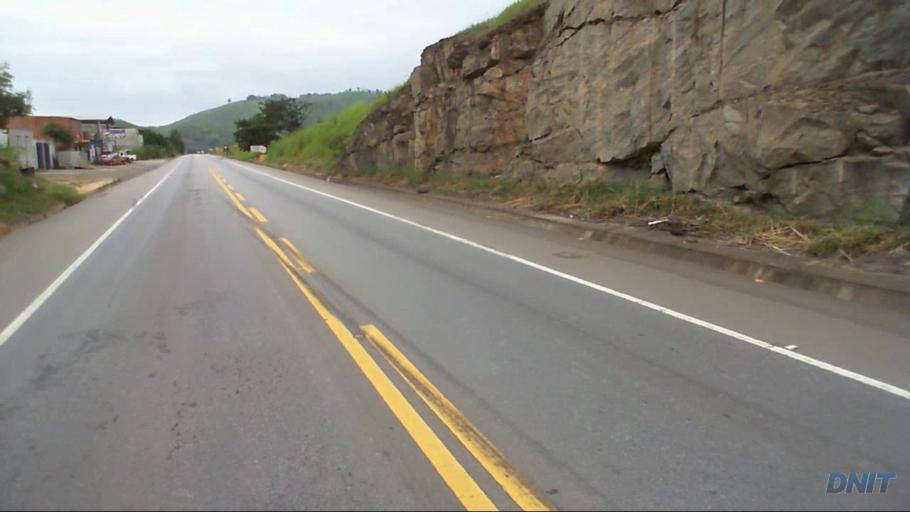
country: BR
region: Minas Gerais
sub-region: Coronel Fabriciano
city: Coronel Fabriciano
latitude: -19.5327
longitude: -42.6230
